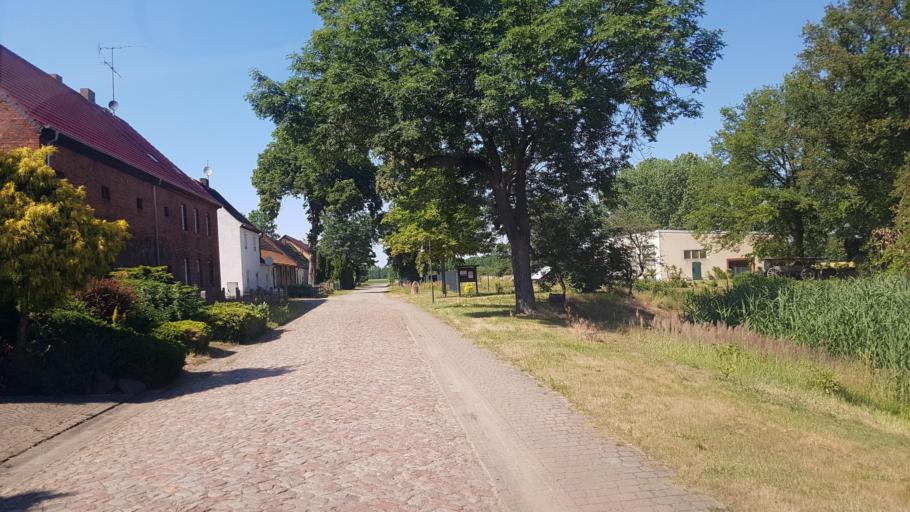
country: DE
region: Saxony-Anhalt
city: Elster
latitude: 51.7708
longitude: 12.8644
